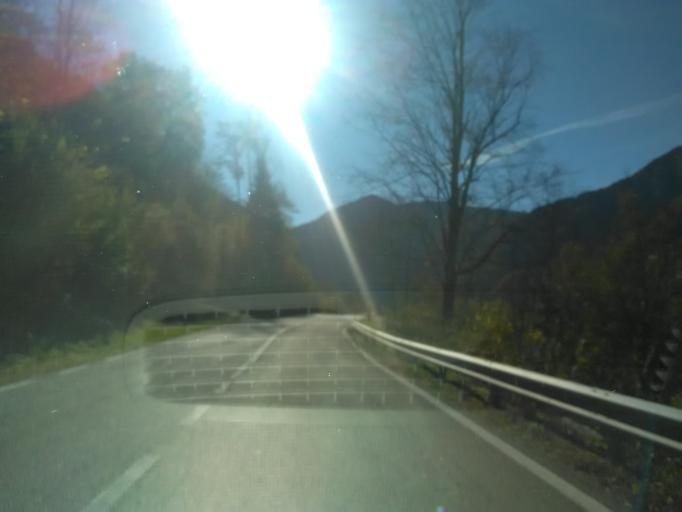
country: IT
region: Piedmont
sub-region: Provincia di Vercelli
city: Campertogno
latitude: 45.7925
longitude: 8.0371
